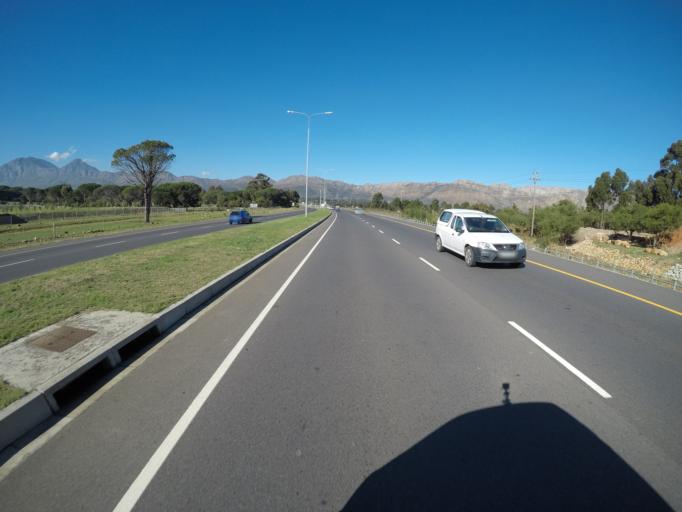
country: ZA
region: Western Cape
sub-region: Overberg District Municipality
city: Grabouw
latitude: -34.1217
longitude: 18.8833
